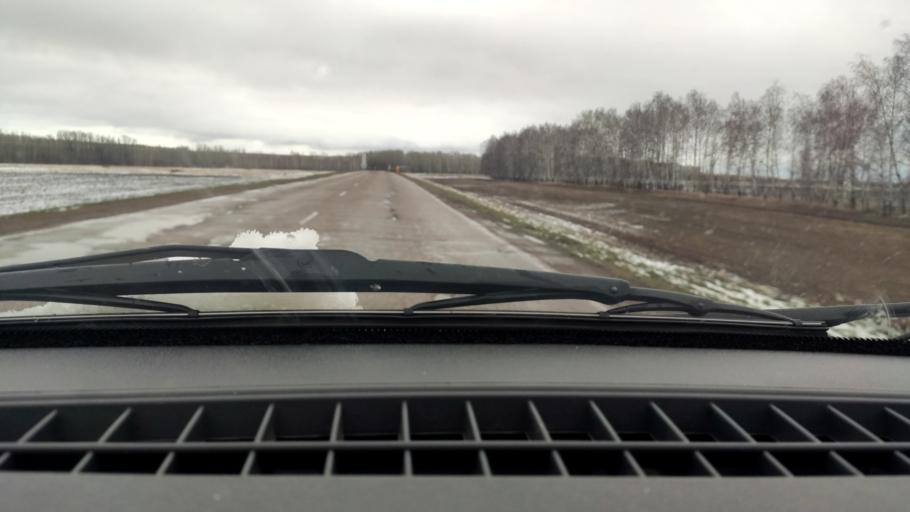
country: RU
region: Bashkortostan
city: Kushnarenkovo
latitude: 55.0861
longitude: 55.0641
